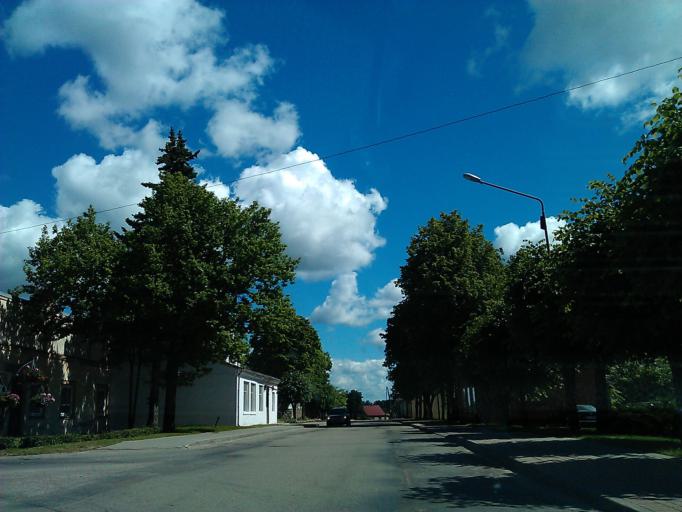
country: LV
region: Varaklani
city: Varaklani
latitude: 56.6099
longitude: 26.7523
